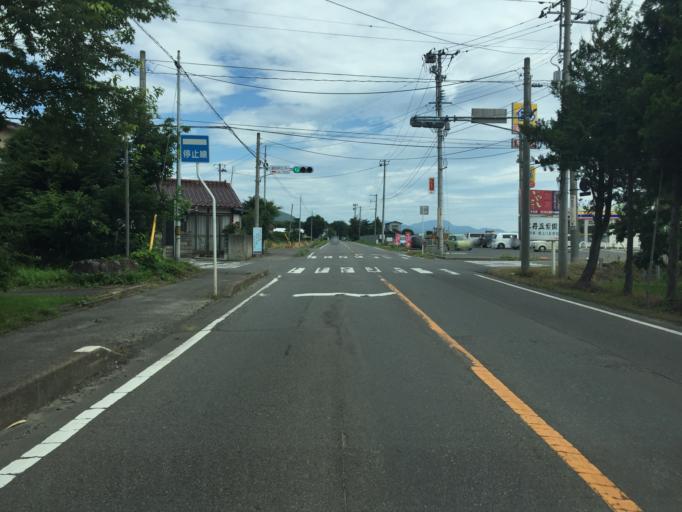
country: JP
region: Fukushima
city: Fukushima-shi
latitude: 37.7759
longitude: 140.3875
